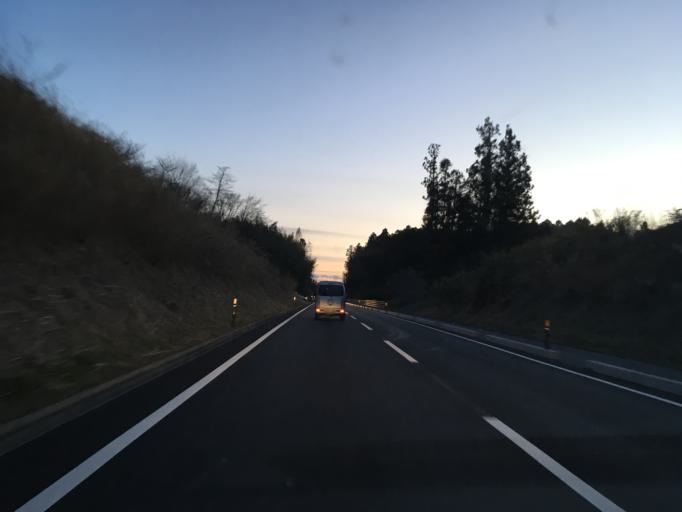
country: JP
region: Miyagi
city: Wakuya
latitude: 38.7262
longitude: 141.2813
